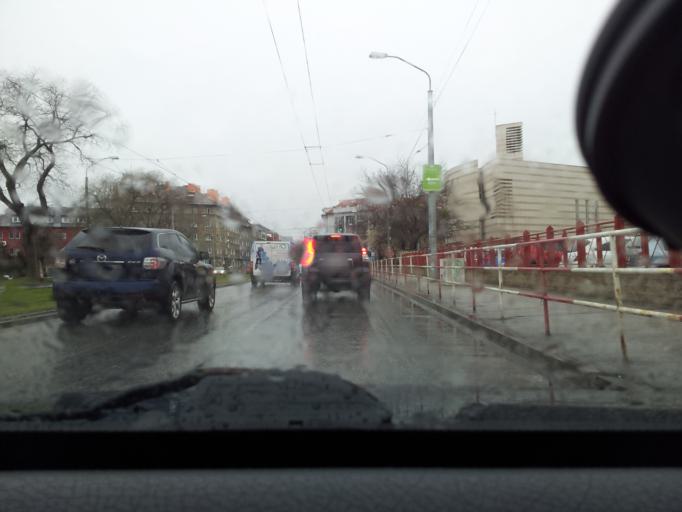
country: SK
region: Bratislavsky
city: Bratislava
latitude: 48.1552
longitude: 17.1360
